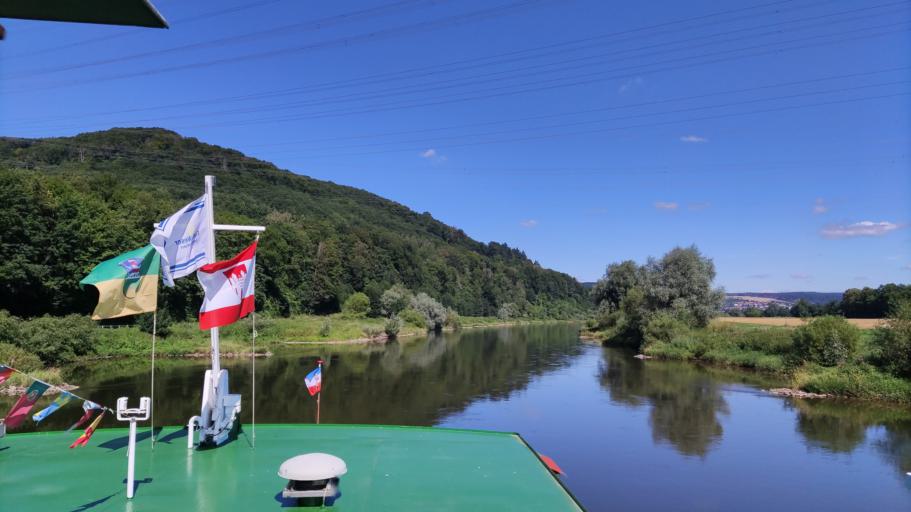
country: DE
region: North Rhine-Westphalia
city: Beverungen
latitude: 51.6403
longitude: 9.3787
